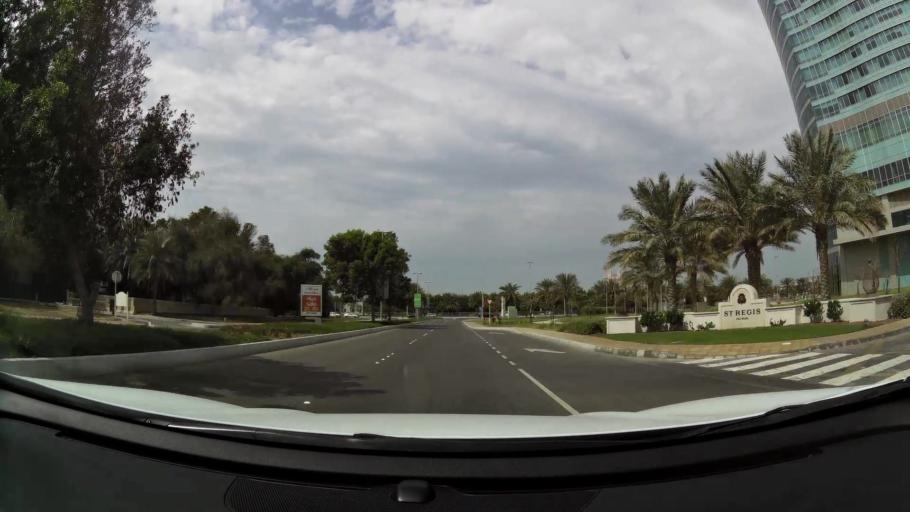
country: AE
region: Abu Dhabi
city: Abu Dhabi
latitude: 24.4634
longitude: 54.3272
